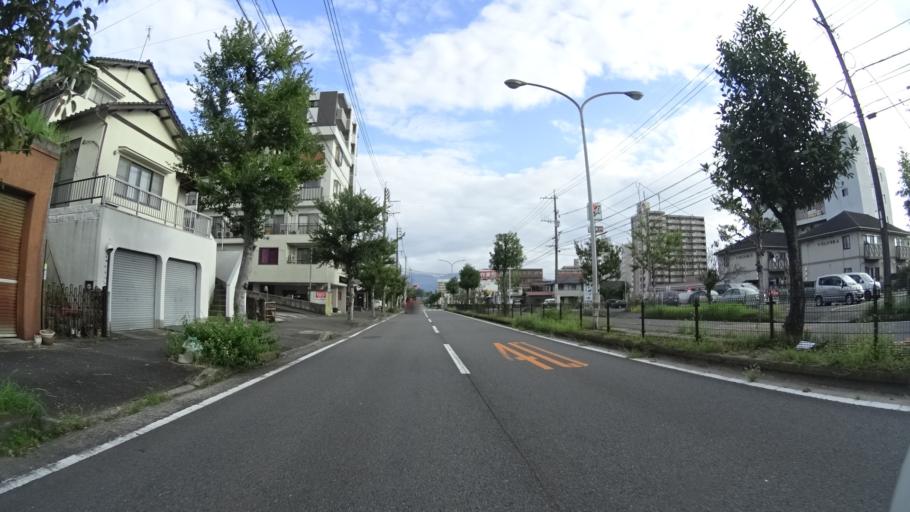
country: JP
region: Oita
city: Beppu
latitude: 33.3001
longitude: 131.4951
